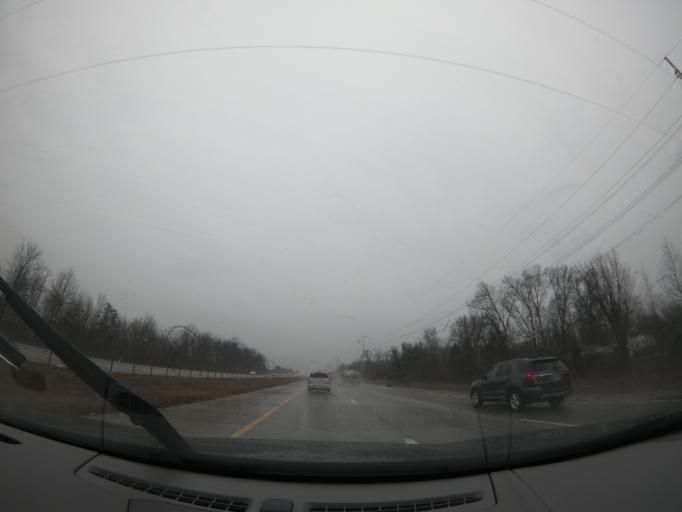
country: US
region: Kentucky
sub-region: Bullitt County
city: Hillview
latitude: 38.0862
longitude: -85.7012
